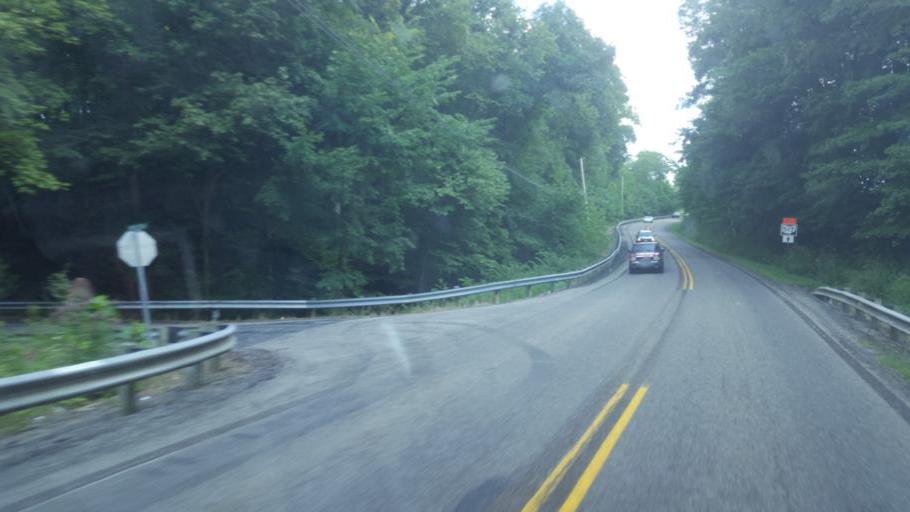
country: US
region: Ohio
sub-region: Columbiana County
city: Lisbon
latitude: 40.7861
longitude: -80.6951
